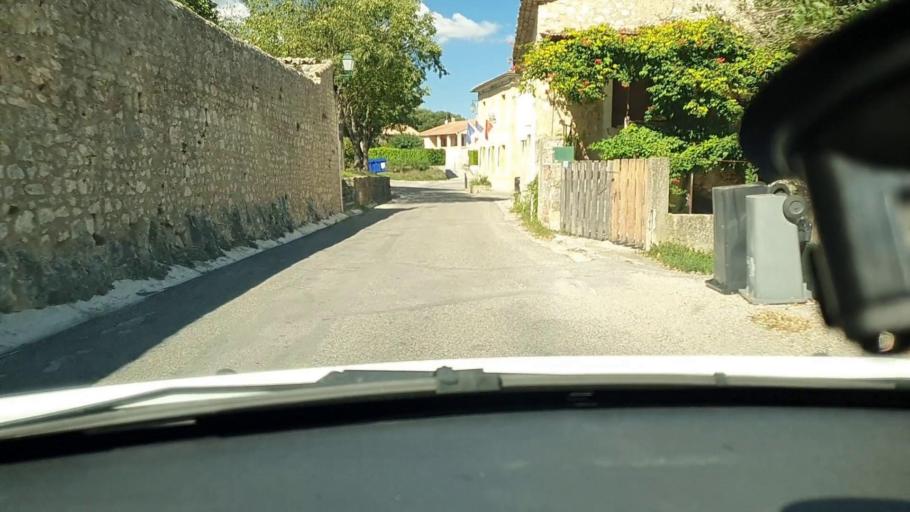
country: FR
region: Languedoc-Roussillon
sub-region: Departement du Gard
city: Goudargues
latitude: 44.1696
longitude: 4.4460
